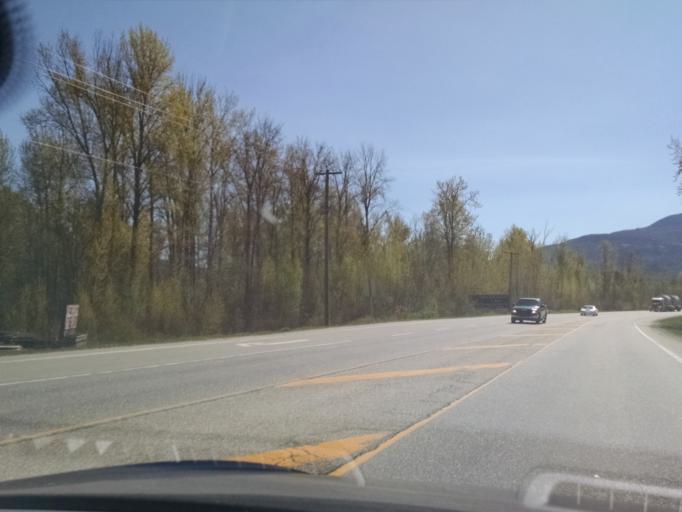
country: CA
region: British Columbia
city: Salmon Arm
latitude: 50.7324
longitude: -119.3167
